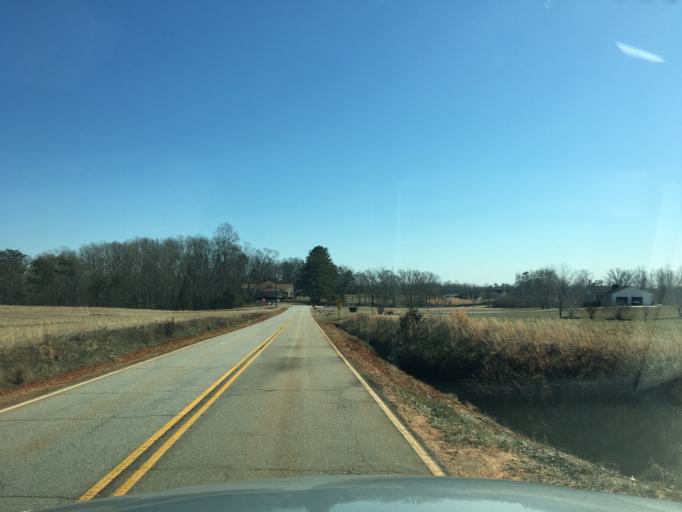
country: US
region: South Carolina
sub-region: Pickens County
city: Liberty
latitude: 34.8181
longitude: -82.7738
